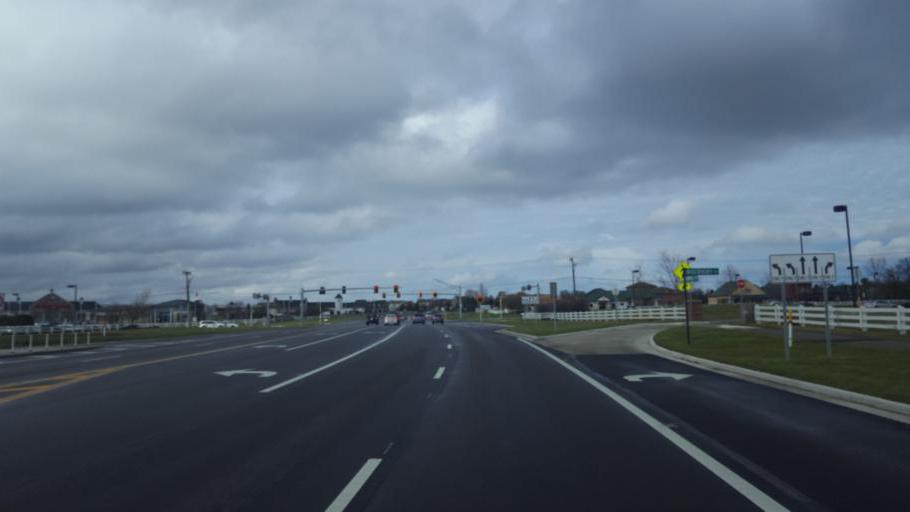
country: US
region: Ohio
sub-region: Delaware County
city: Powell
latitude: 40.1572
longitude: -83.0915
